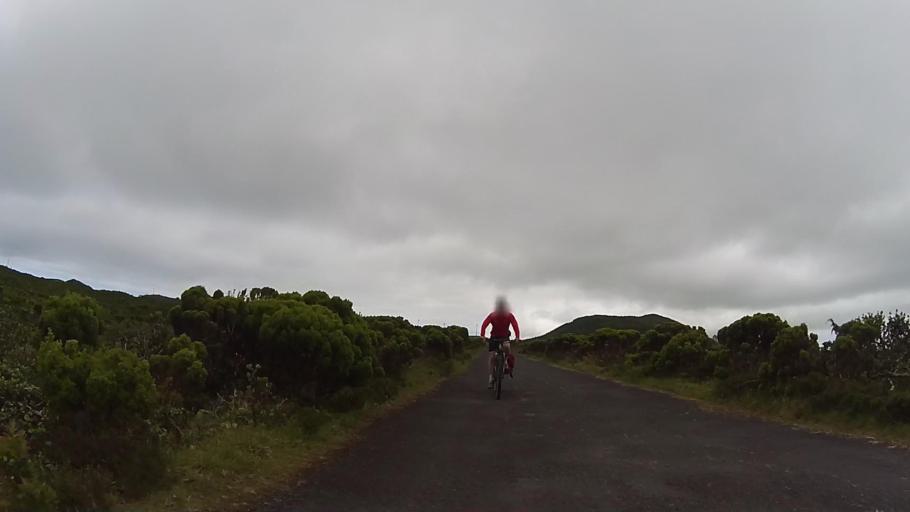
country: PT
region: Azores
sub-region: Sao Roque do Pico
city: Sao Roque do Pico
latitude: 38.4642
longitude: -28.2847
